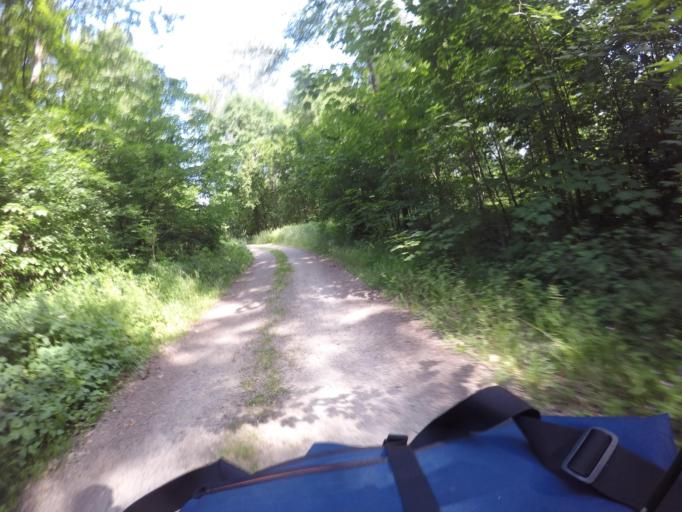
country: DE
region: Baden-Wuerttemberg
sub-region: Karlsruhe Region
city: Otigheim
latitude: 48.9052
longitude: 8.2342
